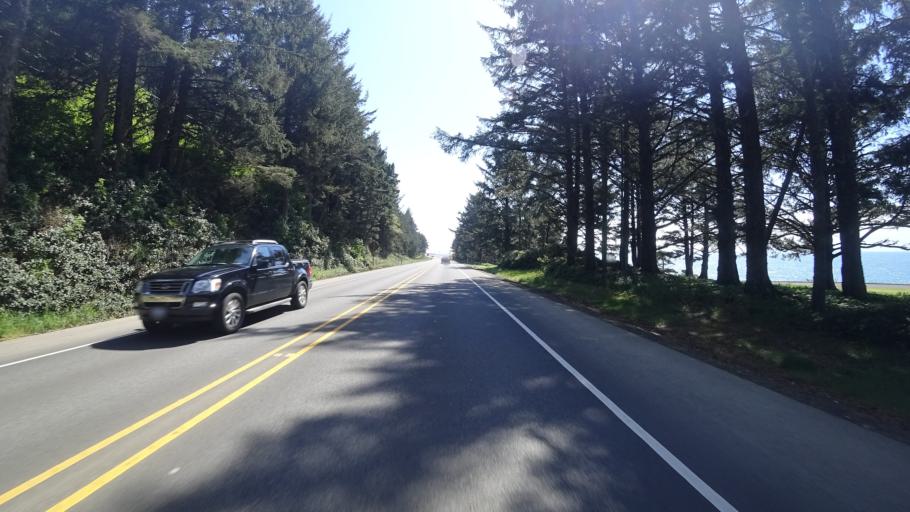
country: US
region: Oregon
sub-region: Lincoln County
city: Depoe Bay
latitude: 44.7848
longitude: -124.0719
